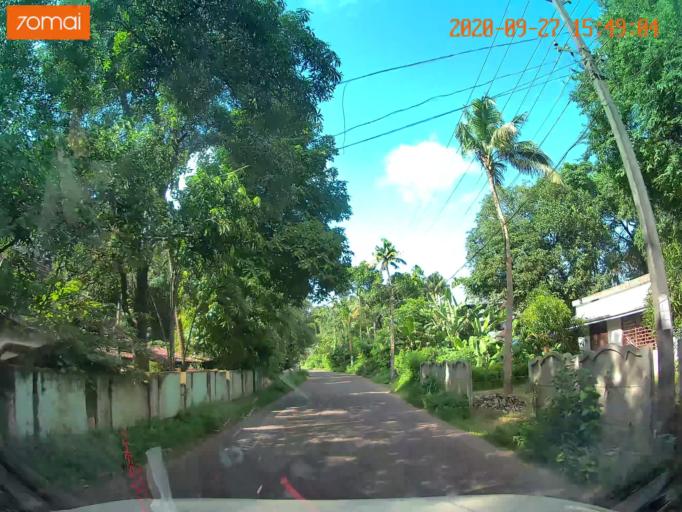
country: IN
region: Kerala
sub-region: Thrissur District
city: Thanniyam
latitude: 10.4868
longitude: 76.1364
